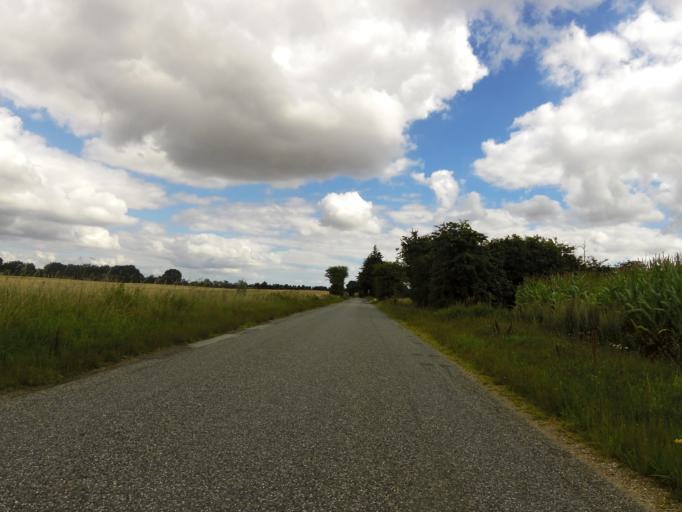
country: DK
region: South Denmark
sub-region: Haderslev Kommune
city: Vojens
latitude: 55.2804
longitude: 9.3134
